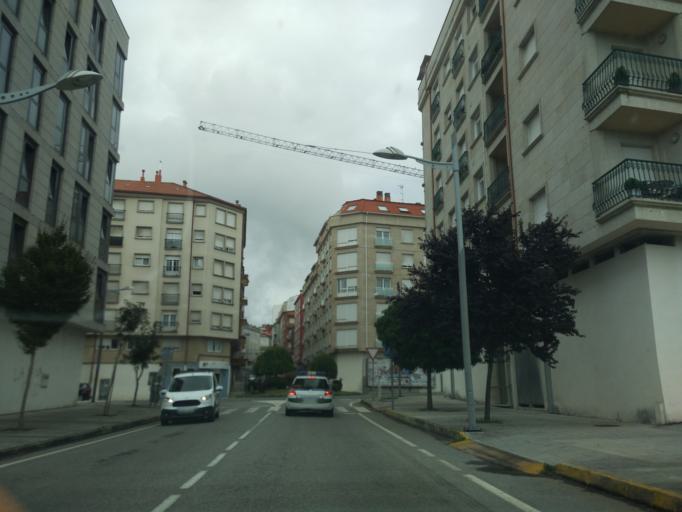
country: ES
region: Galicia
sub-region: Provincia da Coruna
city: Boiro
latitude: 42.6479
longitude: -8.8784
